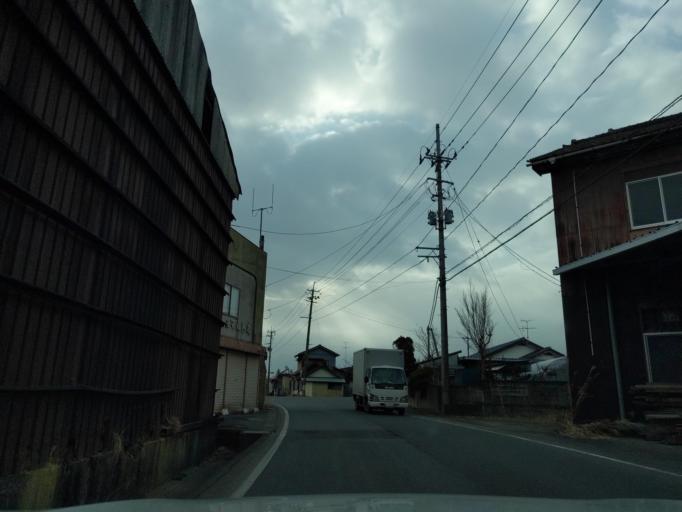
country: JP
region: Fukushima
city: Koriyama
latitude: 37.4519
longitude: 140.3962
